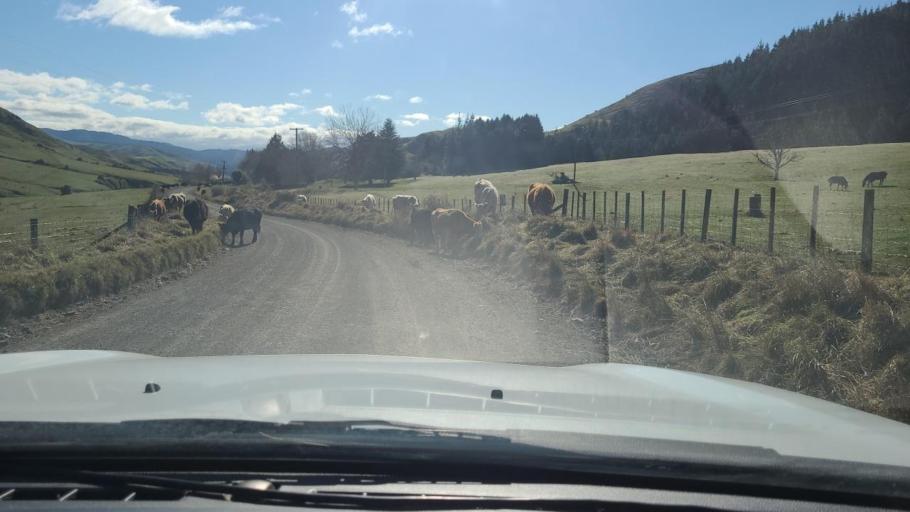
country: NZ
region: Hawke's Bay
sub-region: Napier City
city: Taradale
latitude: -39.2330
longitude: 176.4989
